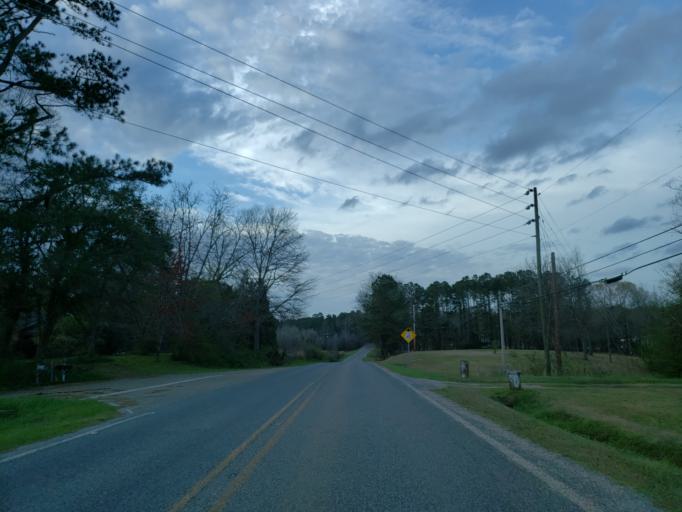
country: US
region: Mississippi
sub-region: Clarke County
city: Stonewall
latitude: 32.2182
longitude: -88.6991
